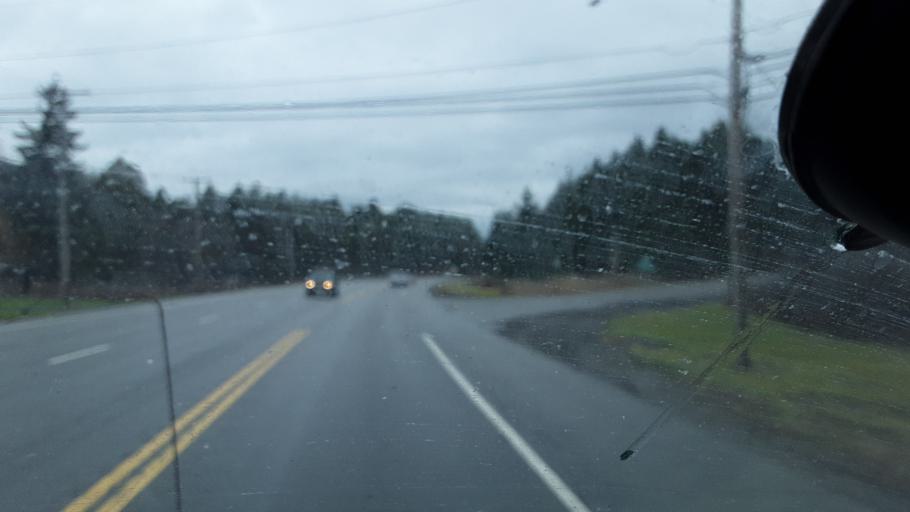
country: US
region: New York
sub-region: Cattaraugus County
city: Yorkshire
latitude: 42.5894
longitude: -78.4945
